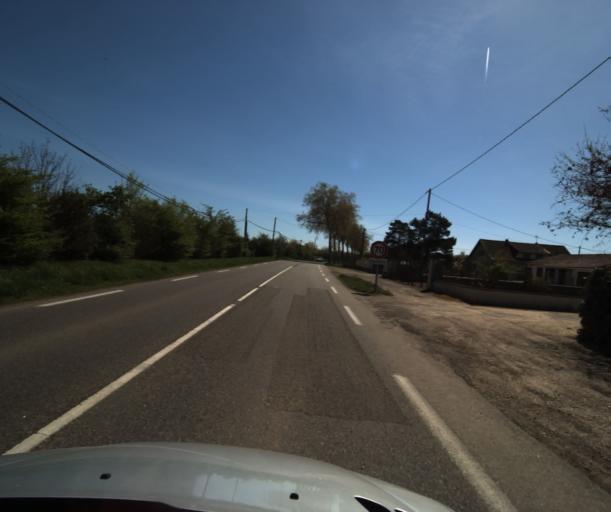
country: FR
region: Midi-Pyrenees
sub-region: Departement du Tarn-et-Garonne
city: Montbeton
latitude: 44.0515
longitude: 1.2957
